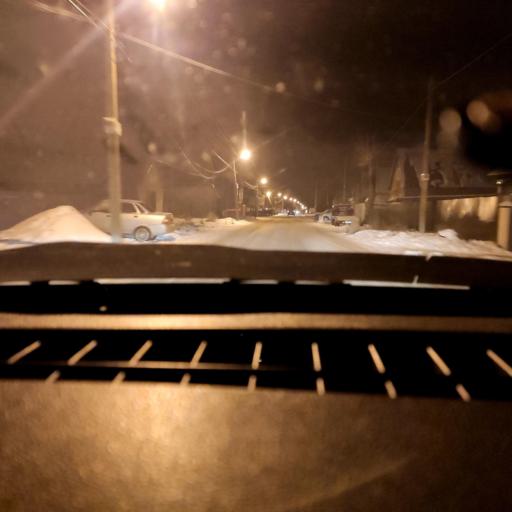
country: RU
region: Bashkortostan
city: Iglino
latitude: 54.8353
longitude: 56.1867
